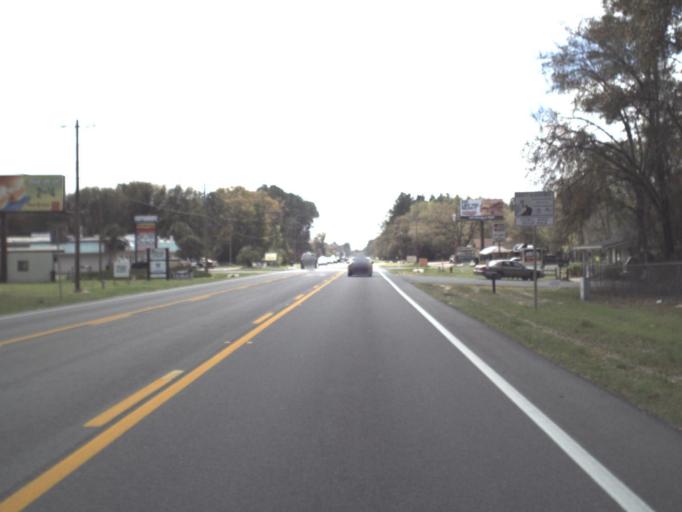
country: US
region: Florida
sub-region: Wakulla County
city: Crawfordville
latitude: 30.2008
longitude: -84.3687
